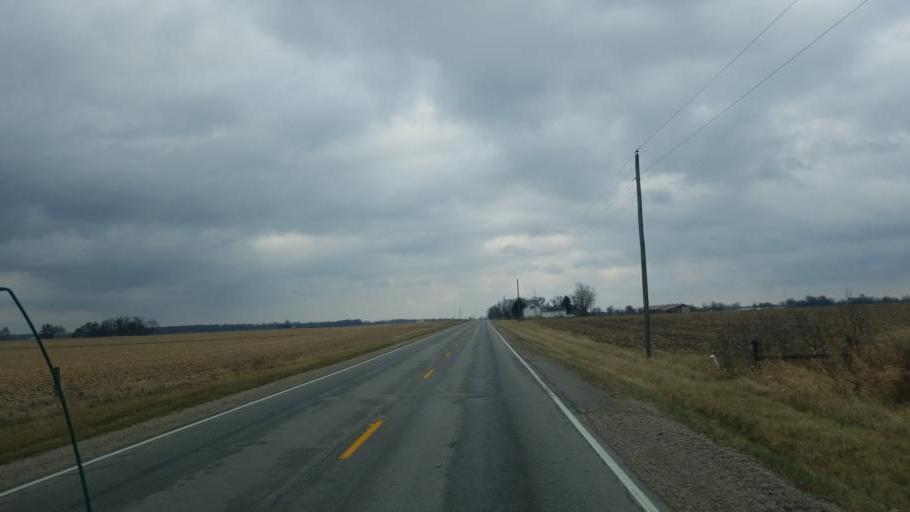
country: US
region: Indiana
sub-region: Adams County
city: Geneva
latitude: 40.5408
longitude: -84.9822
